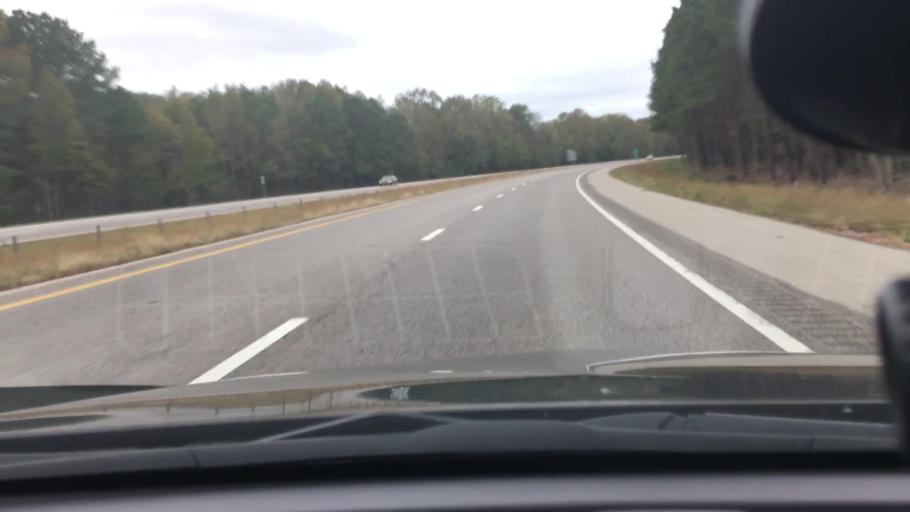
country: US
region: North Carolina
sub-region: Wilson County
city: Wilson
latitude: 35.6689
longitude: -77.8241
